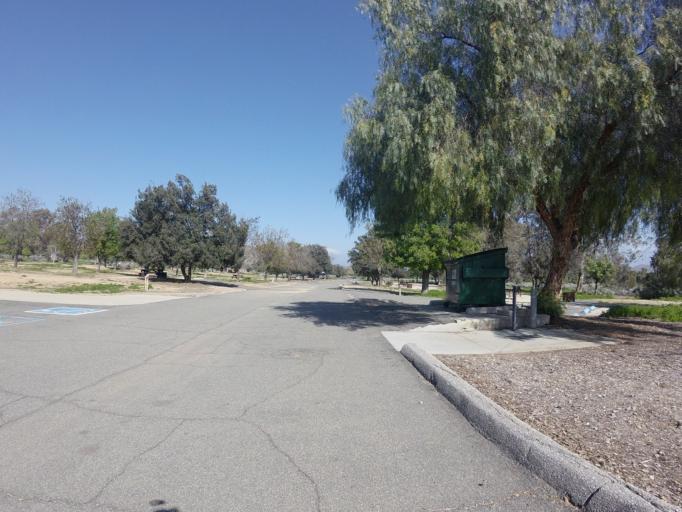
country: US
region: California
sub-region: Riverside County
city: Lakeview
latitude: 33.8738
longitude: -117.1781
